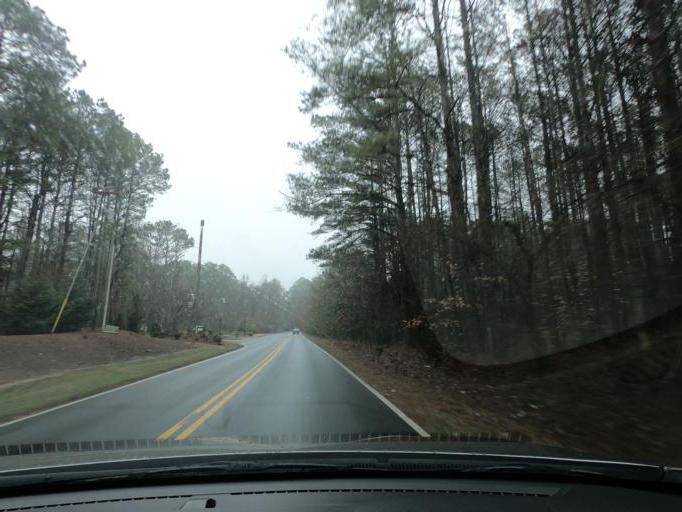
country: US
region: Georgia
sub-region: Fulton County
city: Milton
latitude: 34.1070
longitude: -84.3188
